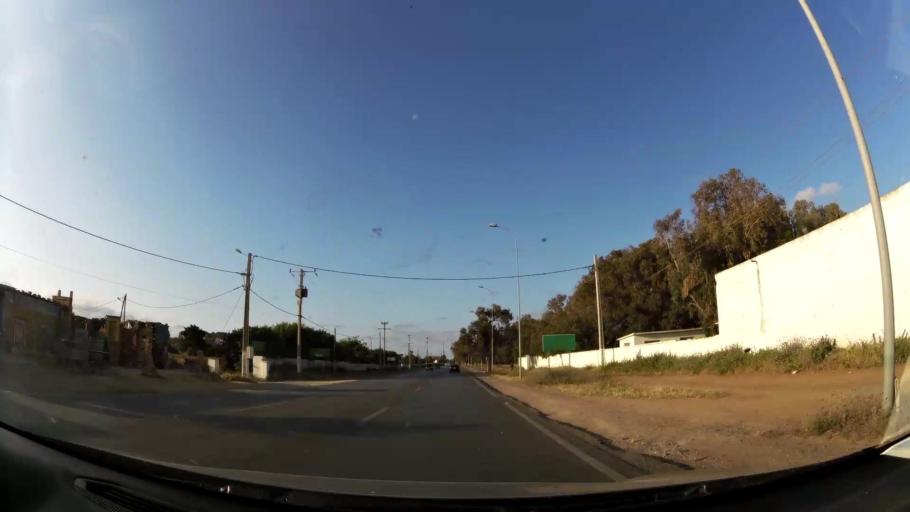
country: MA
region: Rabat-Sale-Zemmour-Zaer
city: Sale
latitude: 34.0991
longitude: -6.7602
